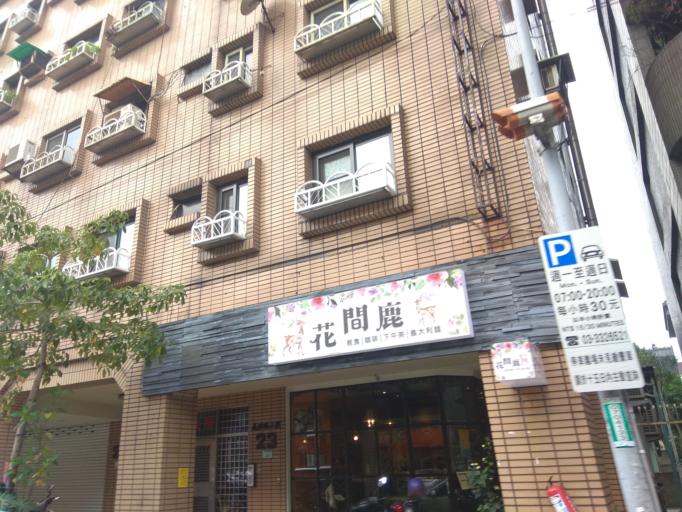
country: TW
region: Taiwan
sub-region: Taoyuan
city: Taoyuan
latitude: 24.9935
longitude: 121.3150
